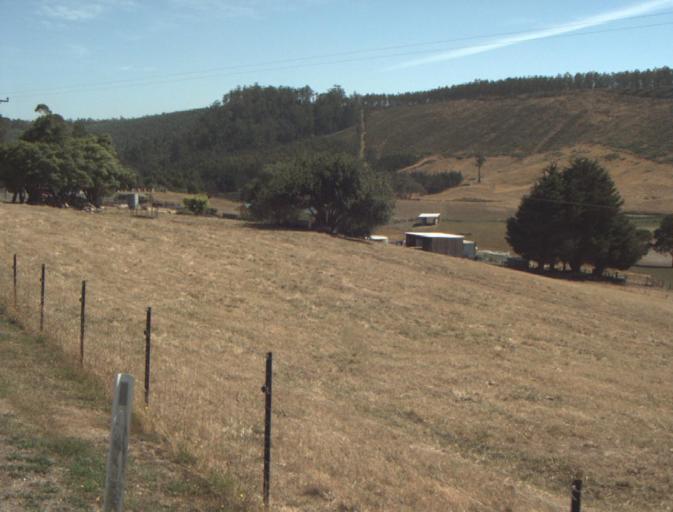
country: AU
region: Tasmania
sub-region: Launceston
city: Mayfield
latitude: -41.2359
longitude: 147.2564
